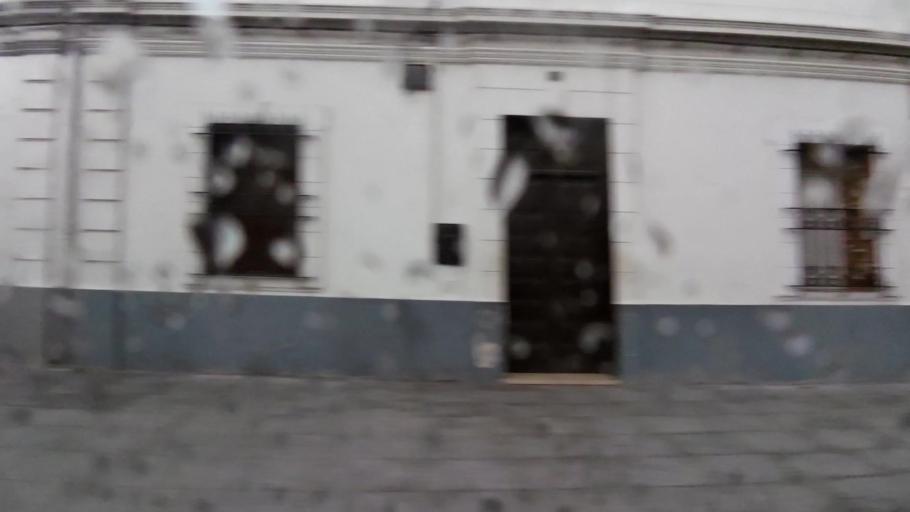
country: MA
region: Doukkala-Abda
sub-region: El-Jadida
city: El Jadida
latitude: 33.2589
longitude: -8.5061
